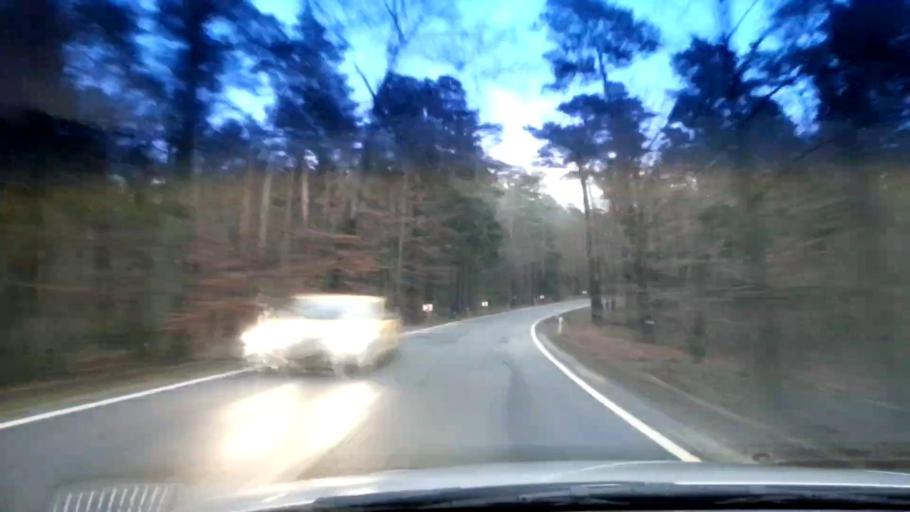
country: DE
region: Bavaria
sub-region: Upper Franconia
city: Pommersfelden
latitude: 49.7906
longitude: 10.7923
